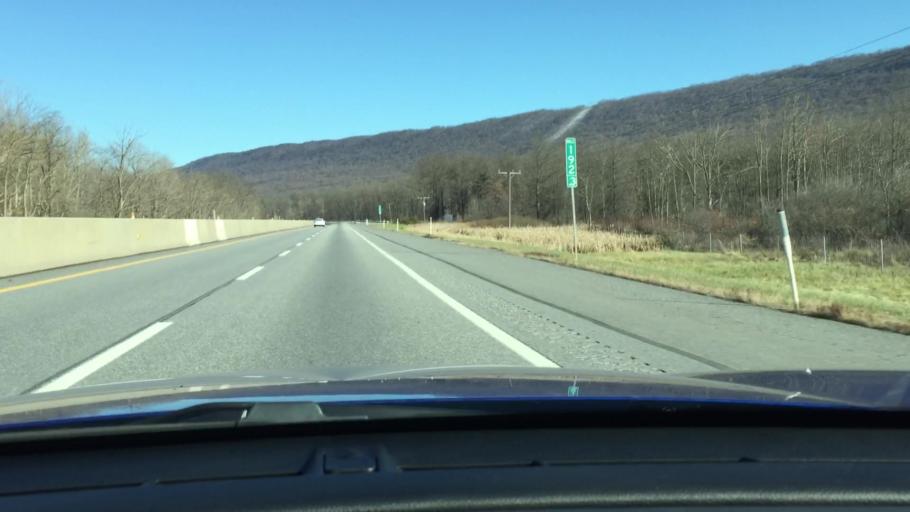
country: US
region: Pennsylvania
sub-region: Franklin County
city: Doylestown
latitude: 40.1256
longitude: -77.7544
